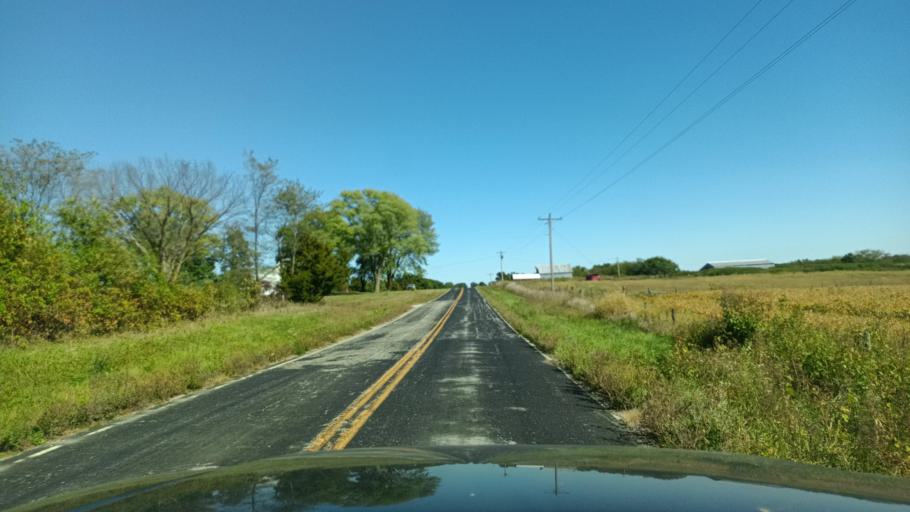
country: US
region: Missouri
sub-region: Macon County
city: La Plata
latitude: 39.9286
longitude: -92.5894
